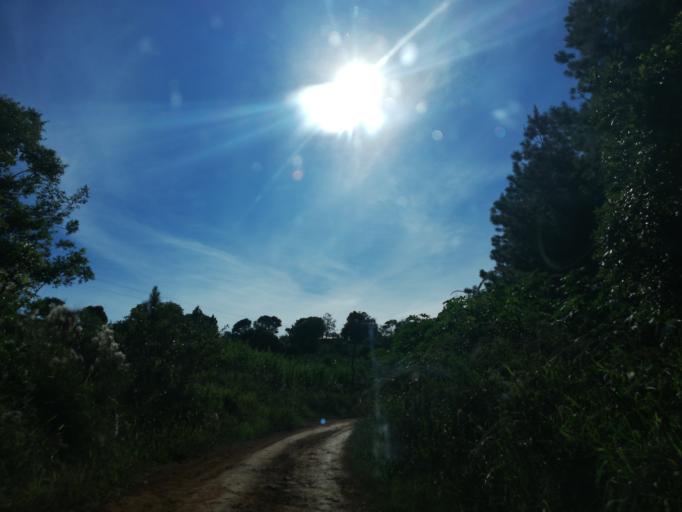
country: AR
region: Misiones
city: Dos de Mayo
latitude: -27.0145
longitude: -54.4463
